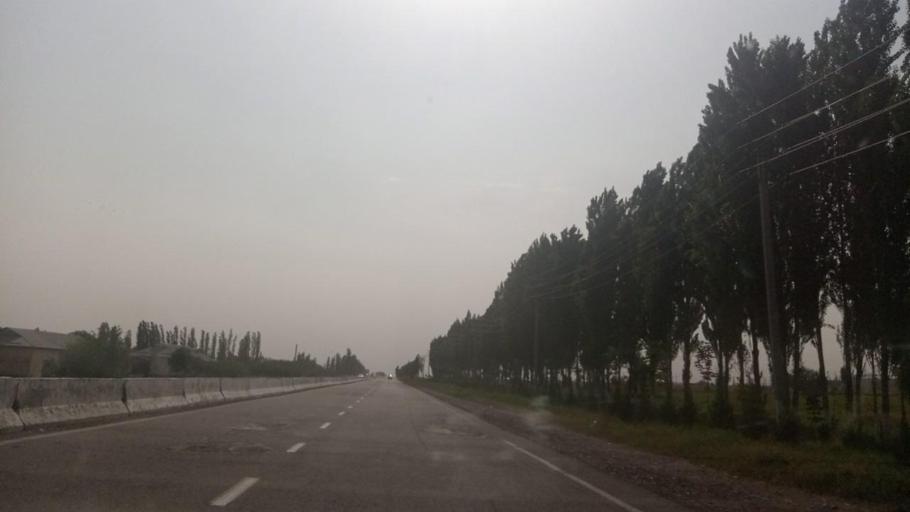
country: UZ
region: Toshkent
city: Ohangaron
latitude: 40.9148
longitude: 69.8242
